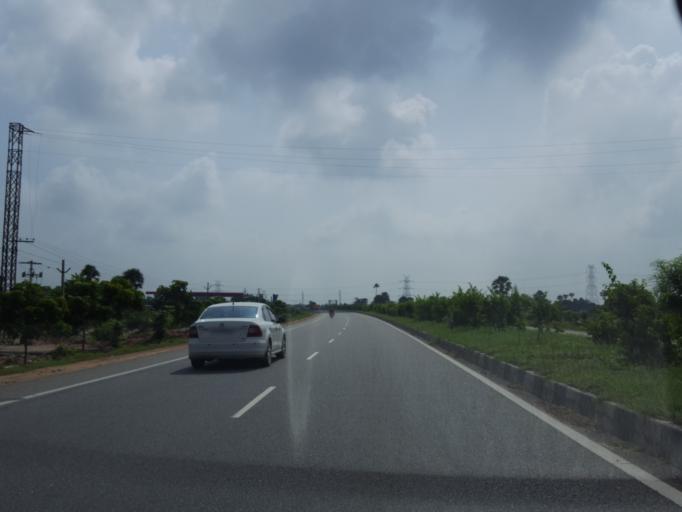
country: IN
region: Telangana
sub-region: Nalgonda
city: Gudur
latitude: 17.2654
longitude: 78.8314
